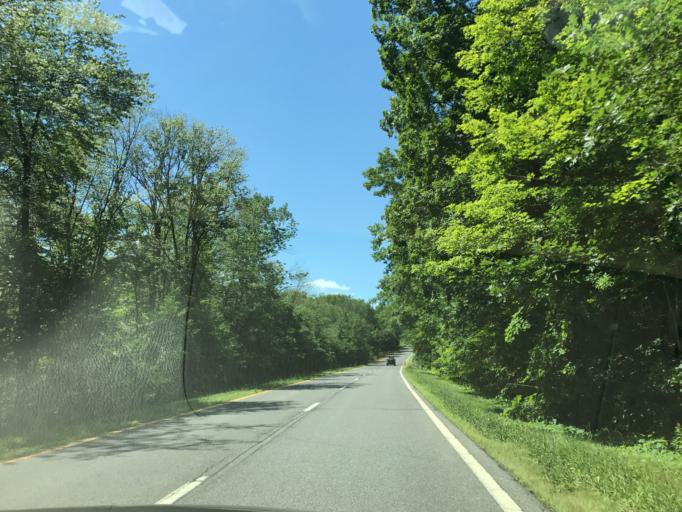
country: US
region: New York
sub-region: Dutchess County
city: Pine Plains
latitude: 41.9379
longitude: -73.7542
